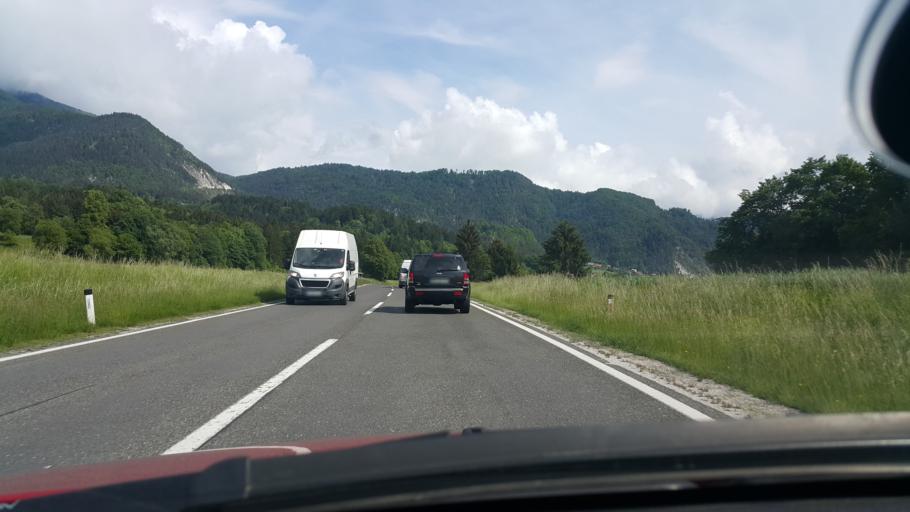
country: SI
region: Trzic
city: Bistrica pri Trzicu
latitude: 46.3427
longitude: 14.2863
